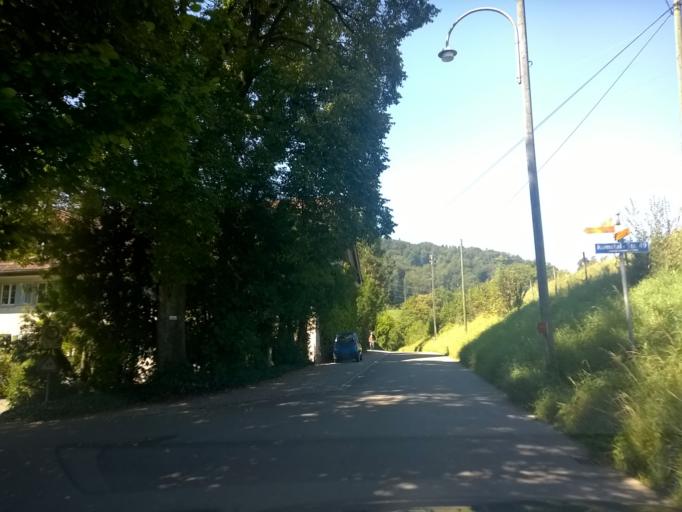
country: CH
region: Zurich
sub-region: Bezirk Winterthur
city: Wuelflingen (Kreis 6) / Niederfeld
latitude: 47.4998
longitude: 8.6657
